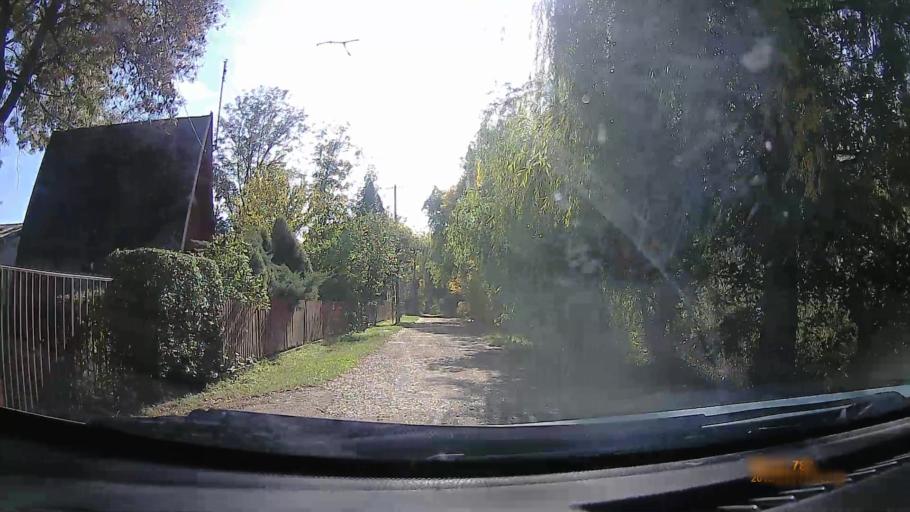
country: HU
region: Hajdu-Bihar
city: Balmazujvaros
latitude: 47.5411
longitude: 21.3269
